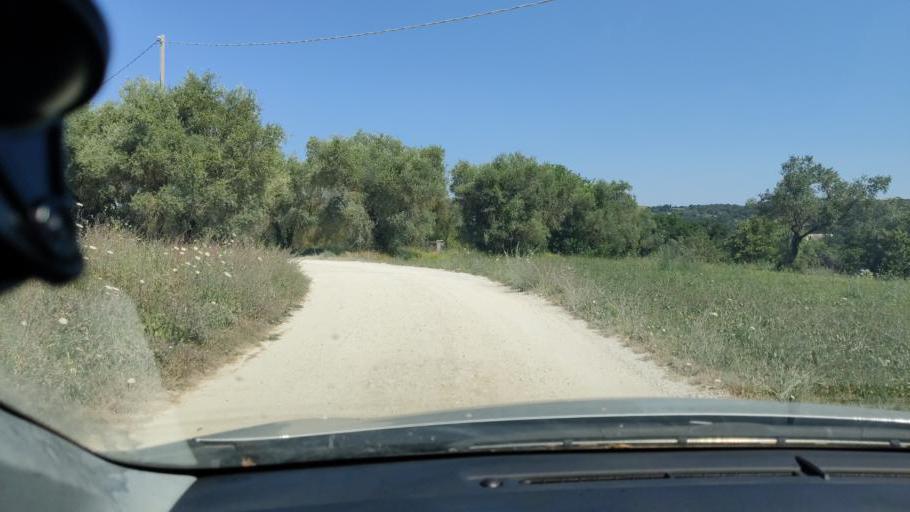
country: IT
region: Umbria
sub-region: Provincia di Terni
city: Fornole
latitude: 42.5452
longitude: 12.4407
